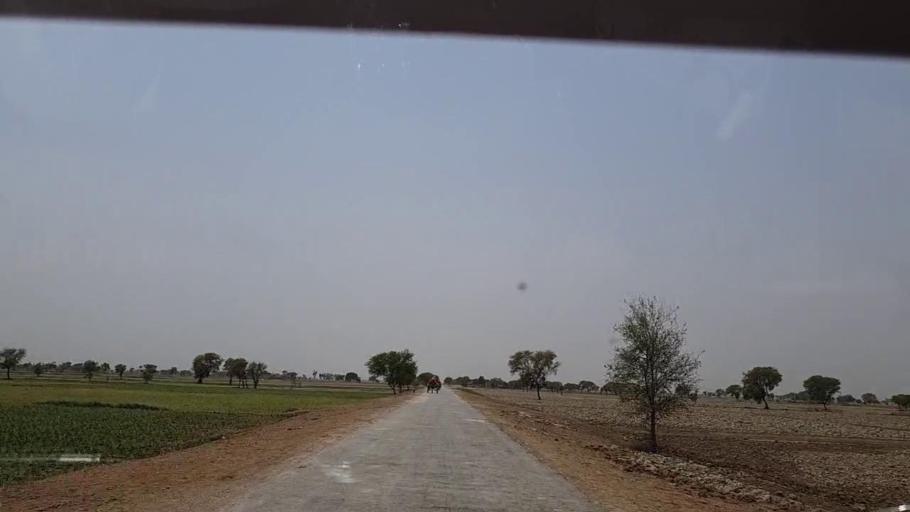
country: PK
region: Sindh
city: Khairpur Nathan Shah
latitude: 27.0059
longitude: 67.6381
